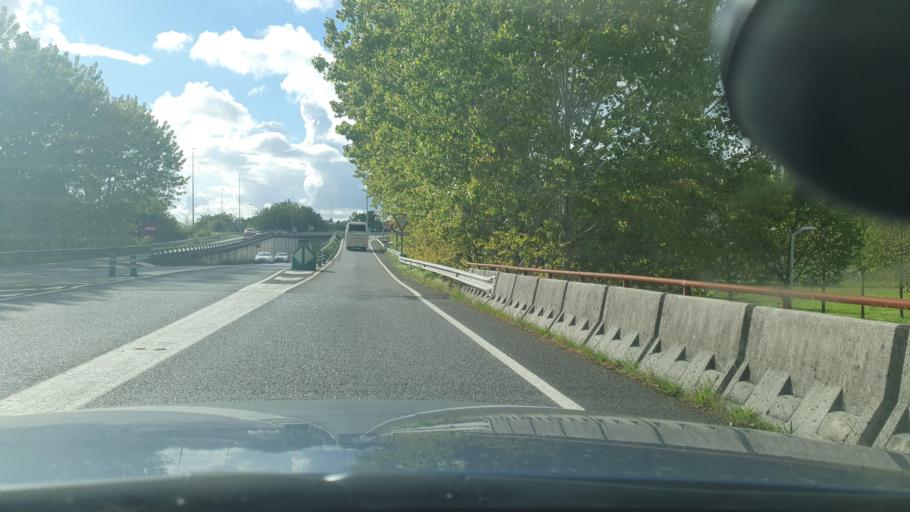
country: ES
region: Galicia
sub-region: Provincia da Coruna
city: Santiago de Compostela
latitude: 42.8685
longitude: -8.5740
